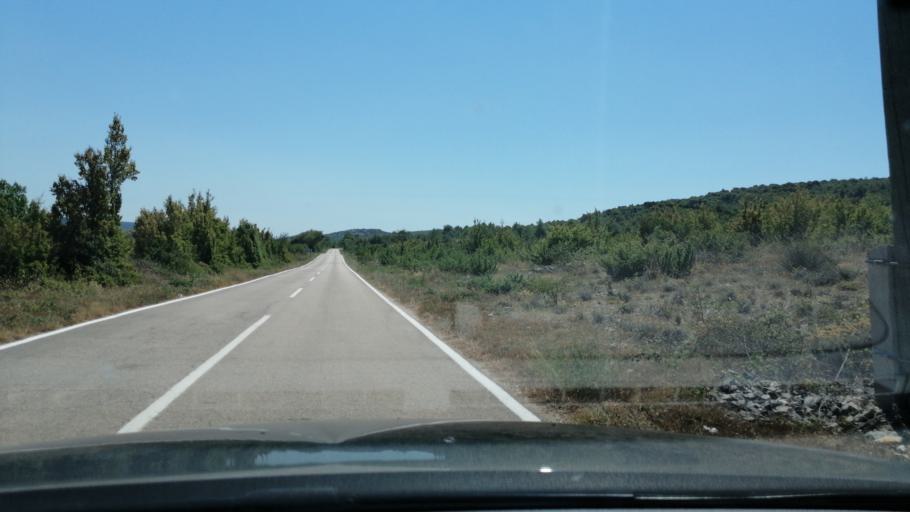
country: HR
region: Sibensko-Kniniska
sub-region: Grad Sibenik
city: Pirovac
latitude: 43.8684
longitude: 15.6831
